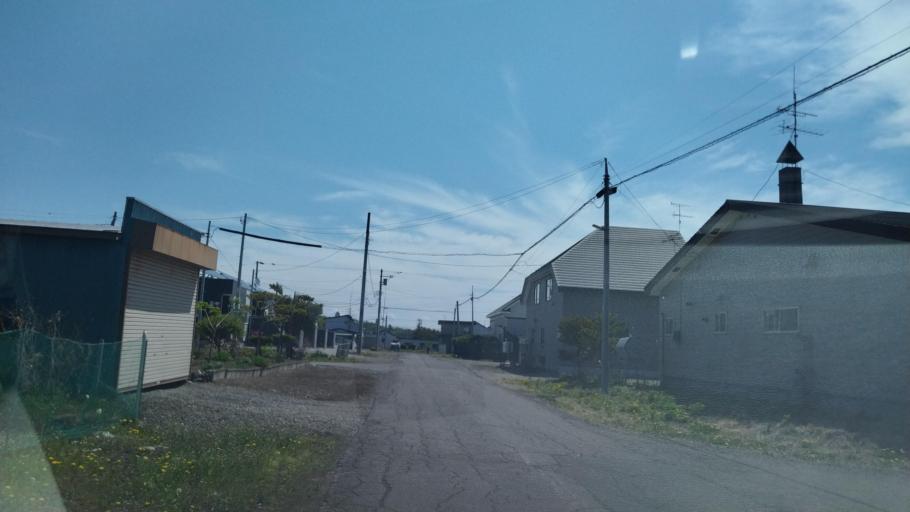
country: JP
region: Hokkaido
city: Otofuke
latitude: 43.2386
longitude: 143.2916
